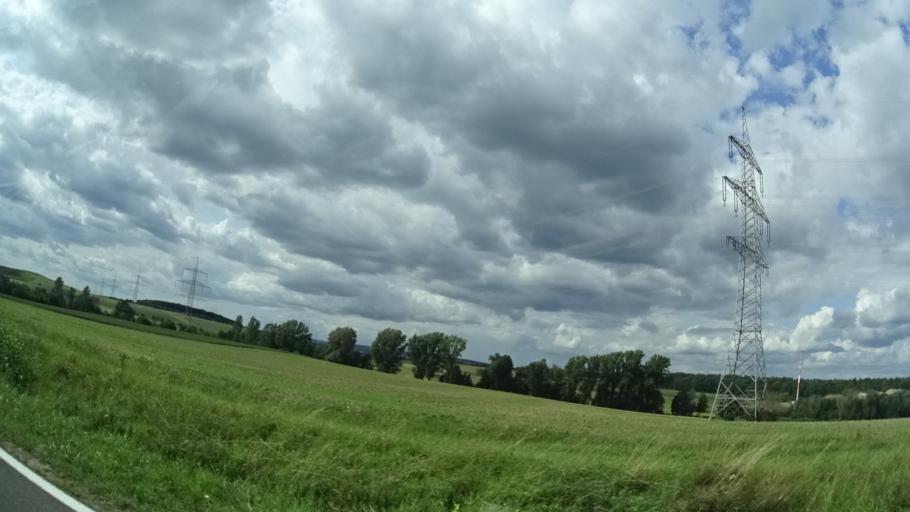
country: DE
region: Bavaria
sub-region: Regierungsbezirk Unterfranken
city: Knetzgau
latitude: 49.9858
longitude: 10.5231
